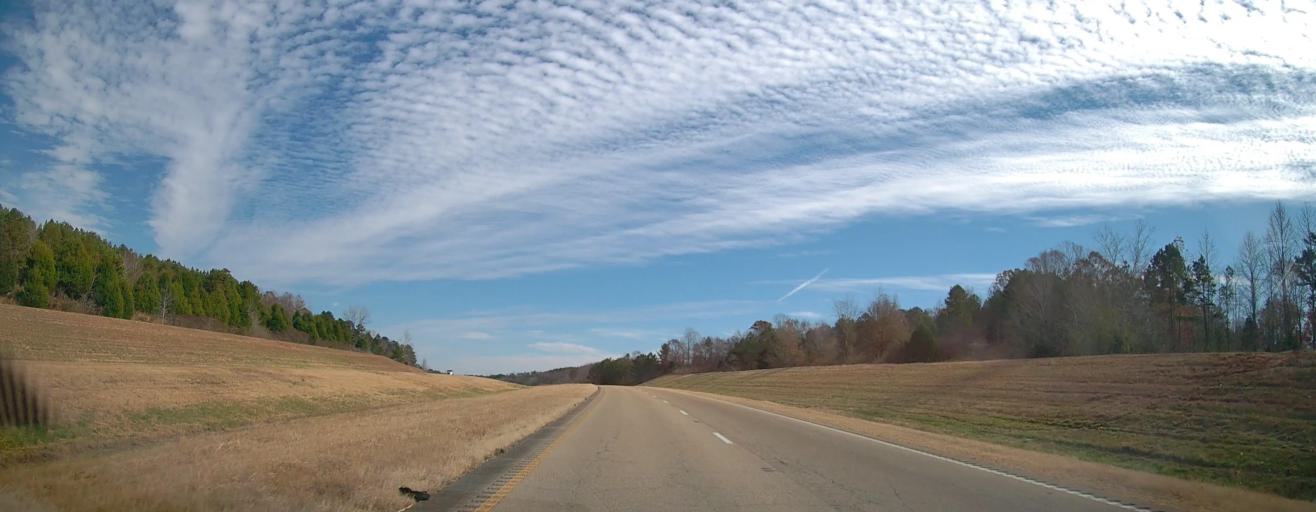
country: US
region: Mississippi
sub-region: Alcorn County
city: Corinth
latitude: 34.9321
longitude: -88.7648
